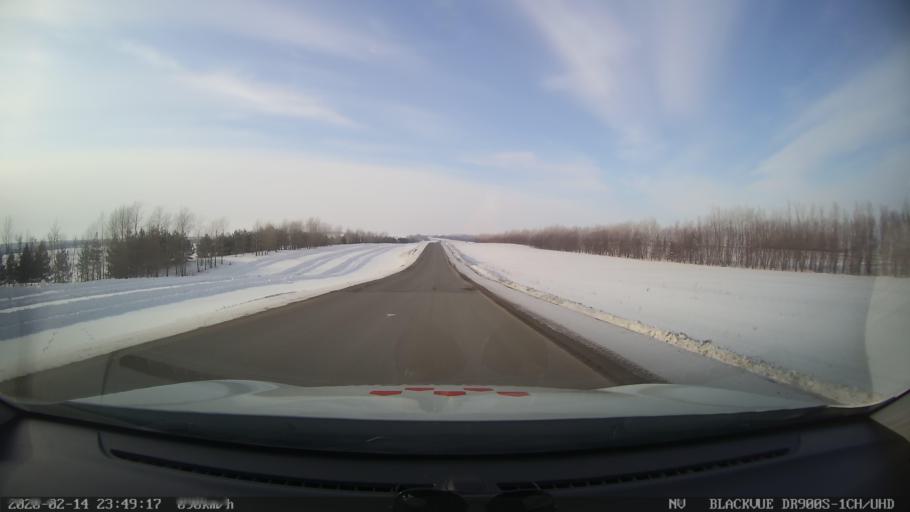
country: RU
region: Tatarstan
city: Kuybyshevskiy Zaton
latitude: 55.2525
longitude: 49.1859
